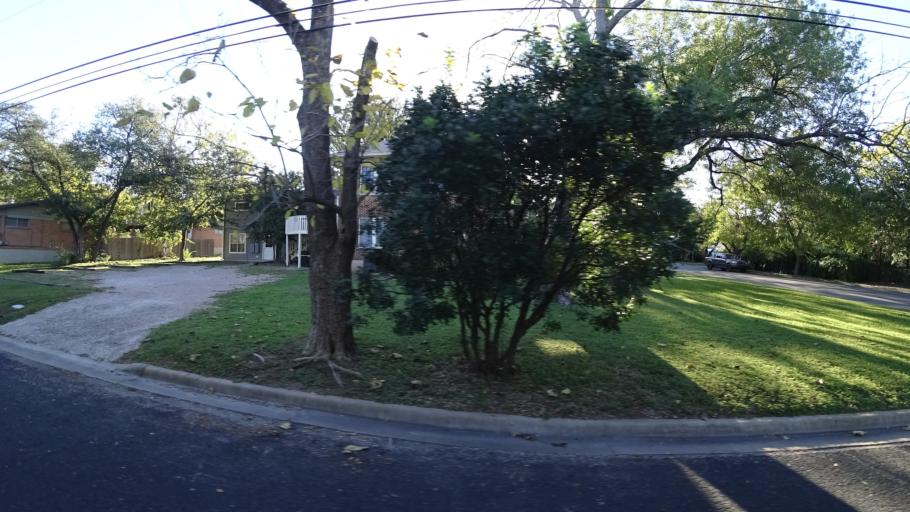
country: US
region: Texas
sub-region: Travis County
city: Austin
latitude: 30.3121
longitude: -97.7252
